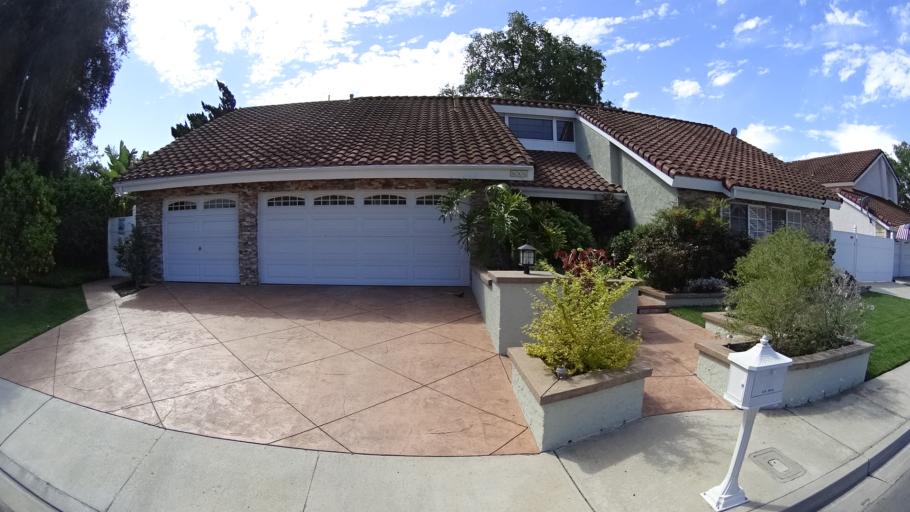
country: US
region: California
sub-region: Ventura County
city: Casa Conejo
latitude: 34.1871
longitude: -118.9374
